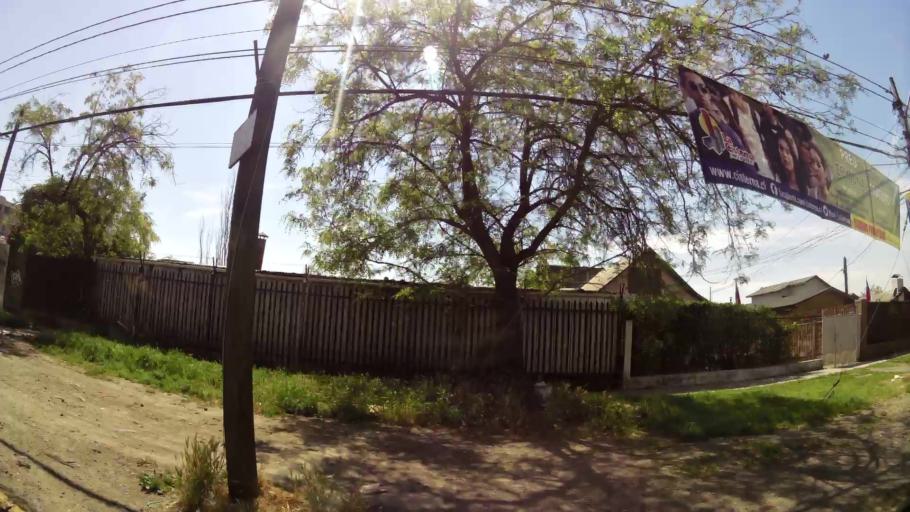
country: CL
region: Santiago Metropolitan
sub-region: Provincia de Santiago
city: La Pintana
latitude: -33.5417
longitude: -70.6574
